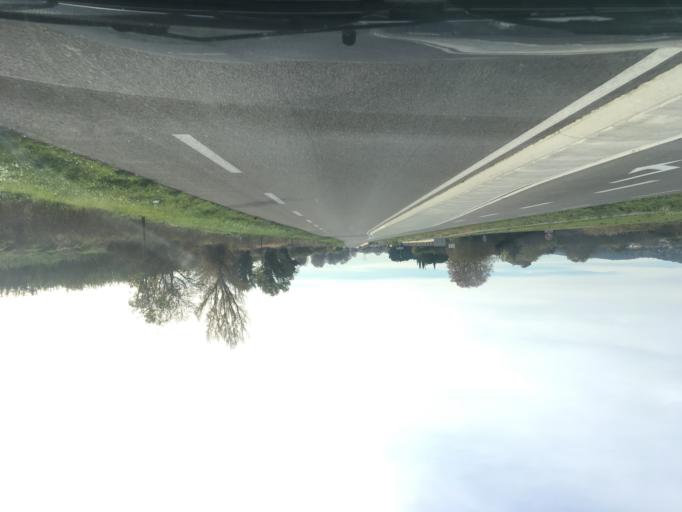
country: FR
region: Provence-Alpes-Cote d'Azur
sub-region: Departement du Vaucluse
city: Villelaure
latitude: 43.7107
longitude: 5.4195
